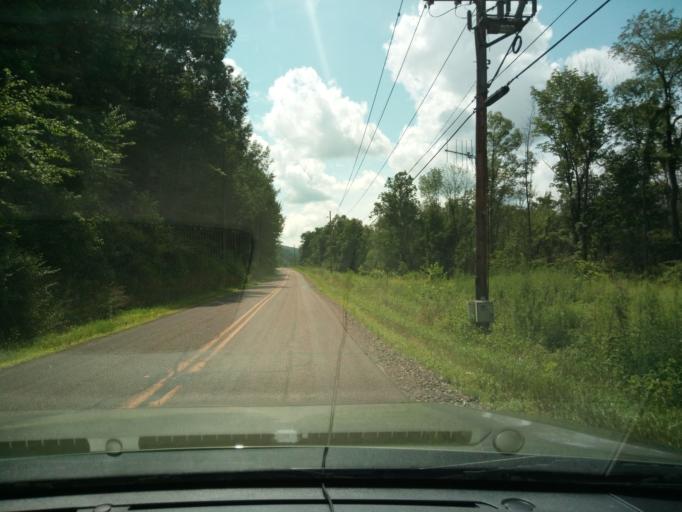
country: US
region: Pennsylvania
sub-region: Bradford County
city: South Waverly
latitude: 41.9958
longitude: -76.5962
